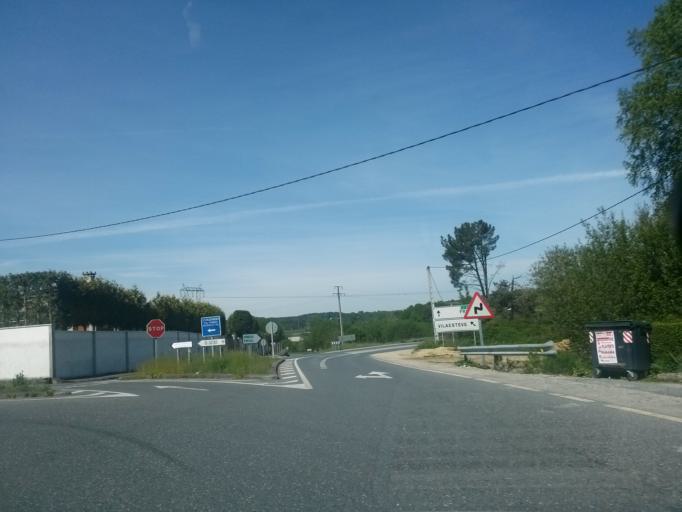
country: ES
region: Galicia
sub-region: Provincia de Lugo
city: Lugo
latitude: 42.9874
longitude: -7.5897
